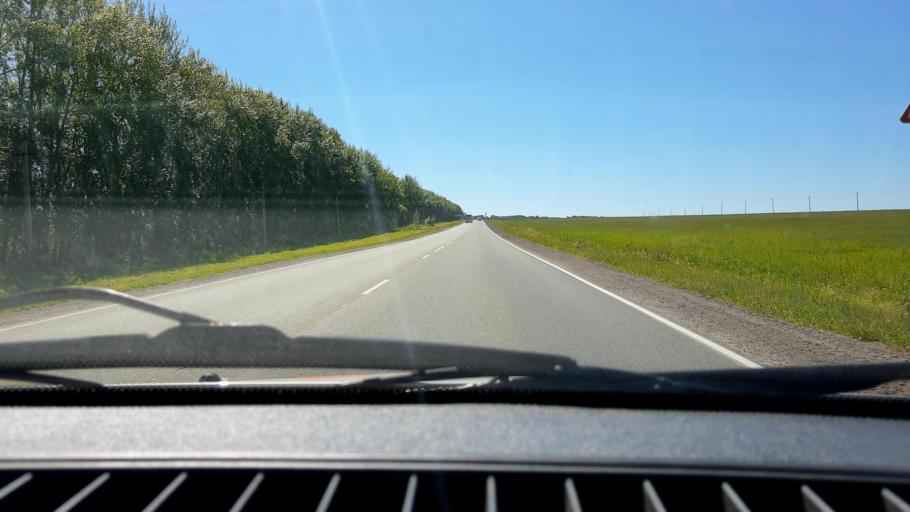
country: RU
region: Bashkortostan
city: Avdon
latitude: 54.5801
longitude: 55.7428
